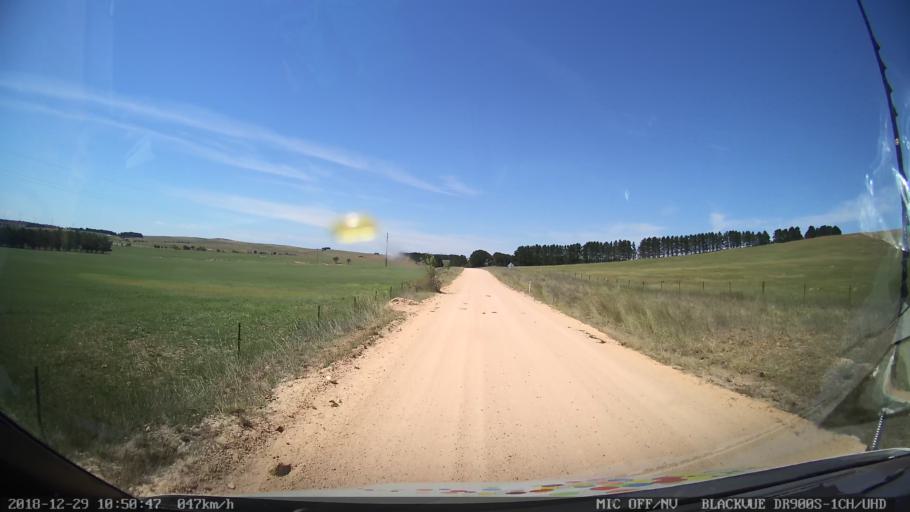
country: AU
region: New South Wales
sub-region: Palerang
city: Bungendore
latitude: -35.0841
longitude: 149.5241
